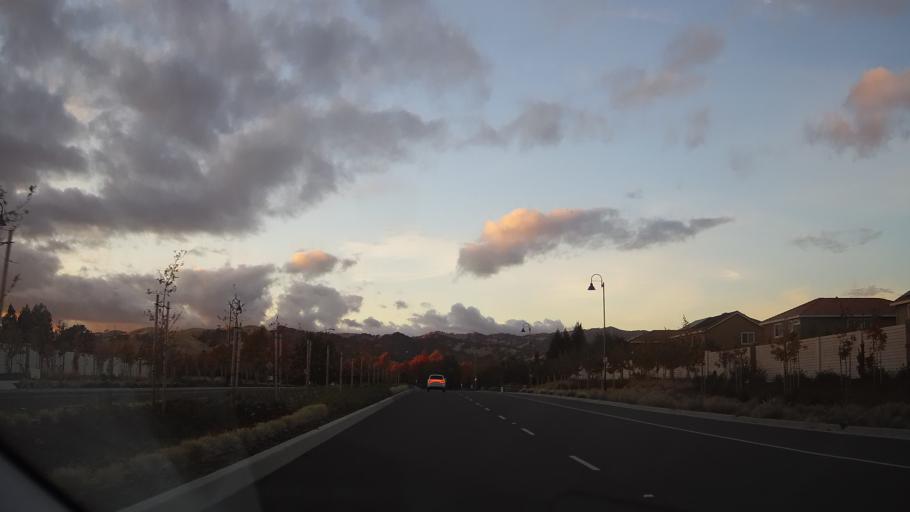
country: US
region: California
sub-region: Solano County
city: Fairfield
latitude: 38.2913
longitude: -122.0140
